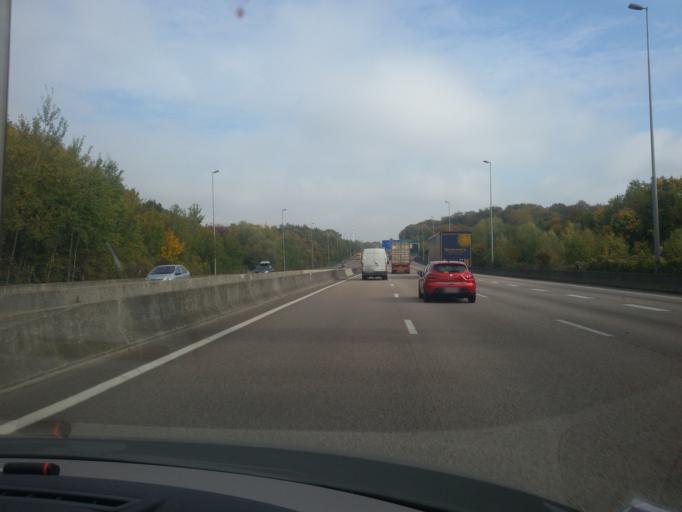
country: FR
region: Haute-Normandie
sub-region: Departement de la Seine-Maritime
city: Grand-Couronne
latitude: 49.3380
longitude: 0.9749
